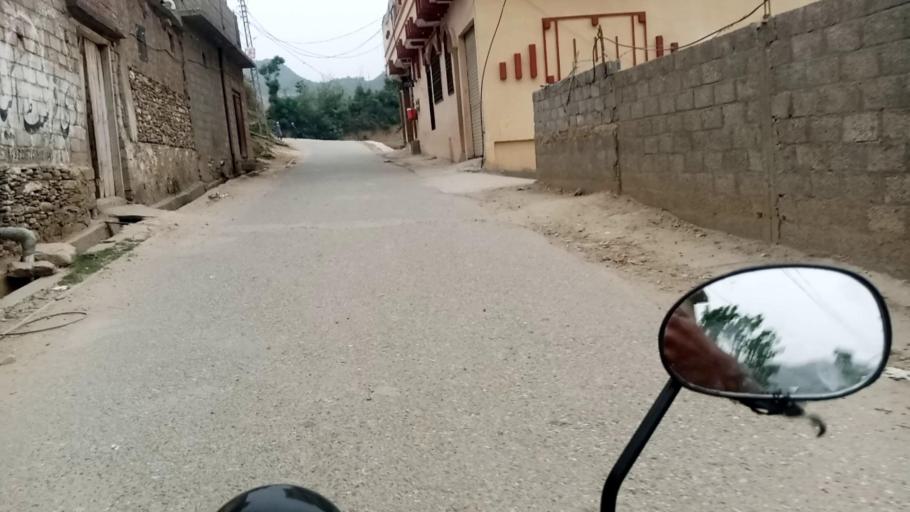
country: PK
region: Khyber Pakhtunkhwa
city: Saidu Sharif
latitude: 34.7568
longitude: 72.3788
